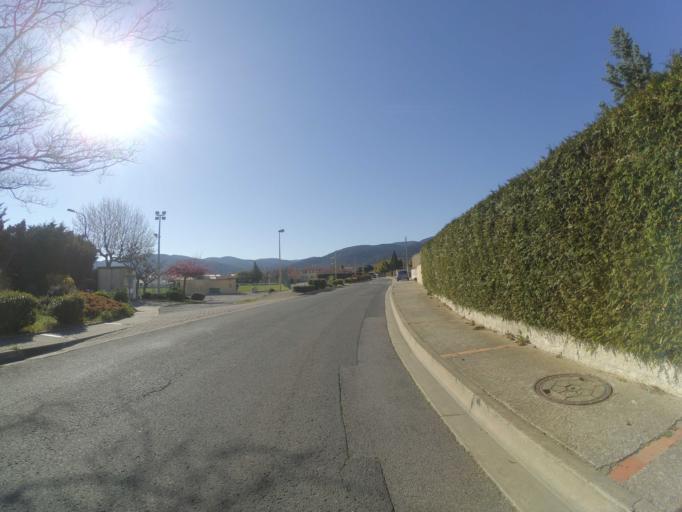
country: FR
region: Languedoc-Roussillon
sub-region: Departement des Pyrenees-Orientales
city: Ille-sur-Tet
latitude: 42.6663
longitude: 2.6152
